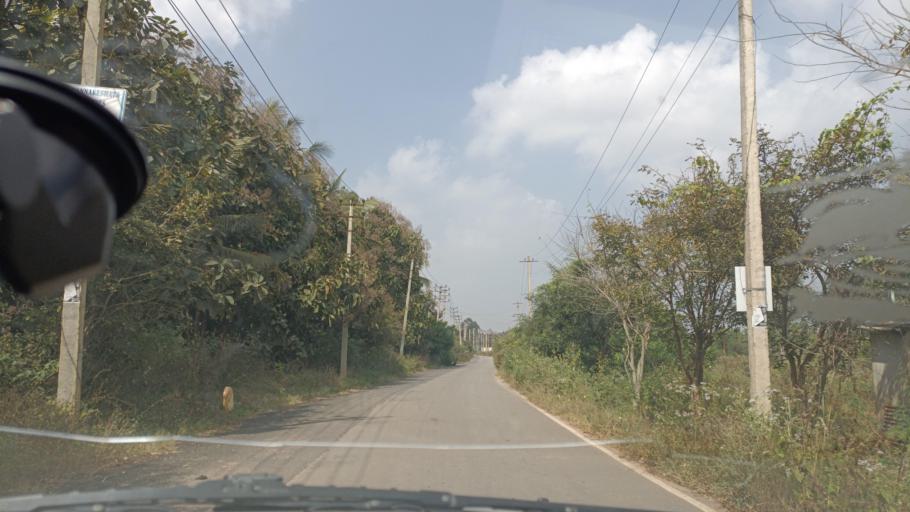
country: IN
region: Karnataka
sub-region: Bangalore Urban
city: Yelahanka
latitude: 13.1512
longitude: 77.6325
